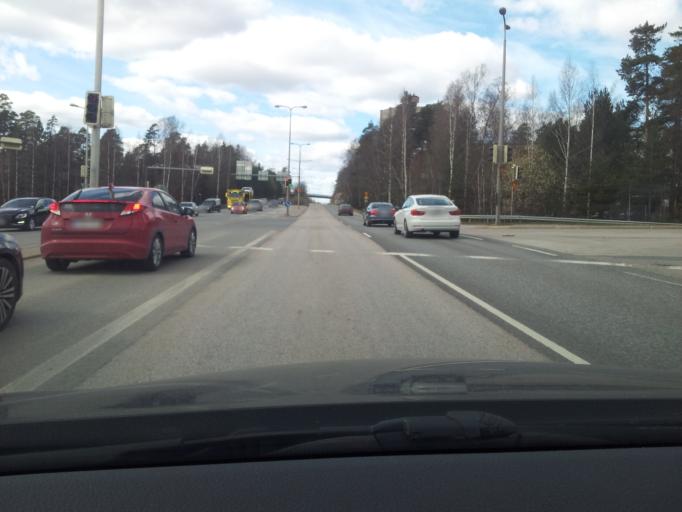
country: FI
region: Uusimaa
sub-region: Helsinki
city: Otaniemi
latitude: 60.1791
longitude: 24.8241
